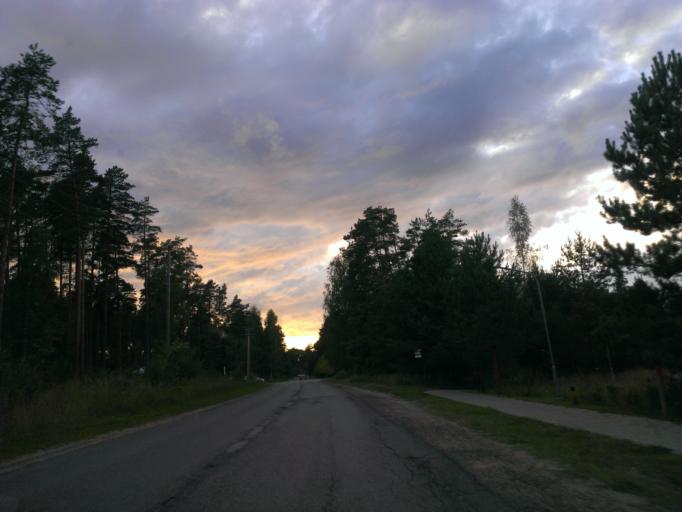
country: LV
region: Riga
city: Bergi
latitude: 56.9862
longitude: 24.3117
